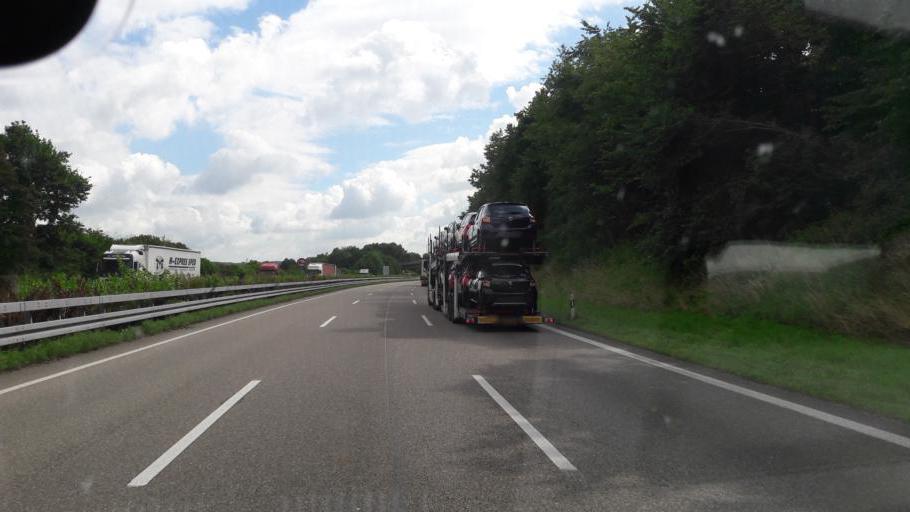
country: DE
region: Baden-Wuerttemberg
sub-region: Regierungsbezirk Stuttgart
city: Bretzfeld
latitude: 49.1922
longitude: 9.4215
